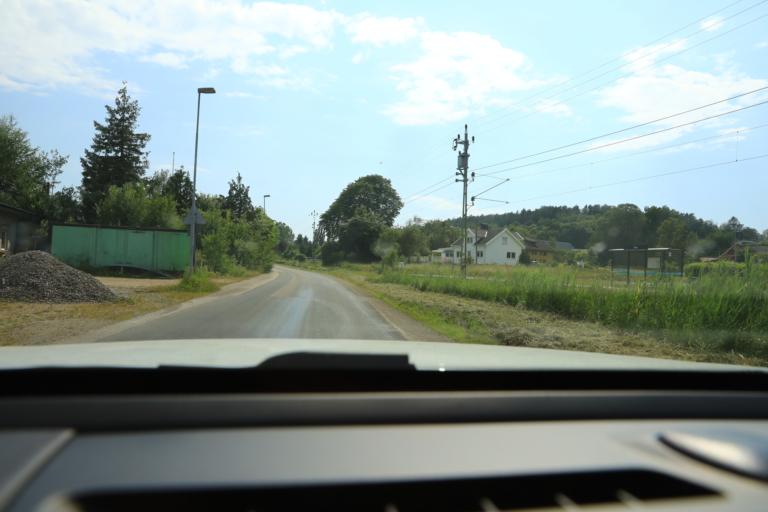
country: SE
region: Halland
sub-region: Varbergs Kommun
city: Varberg
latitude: 57.1735
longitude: 12.3008
